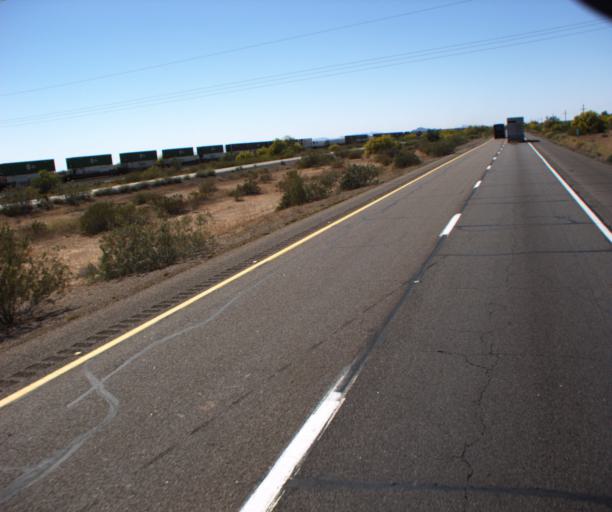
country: US
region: Arizona
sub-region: Maricopa County
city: Gila Bend
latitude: 32.8437
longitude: -113.2963
